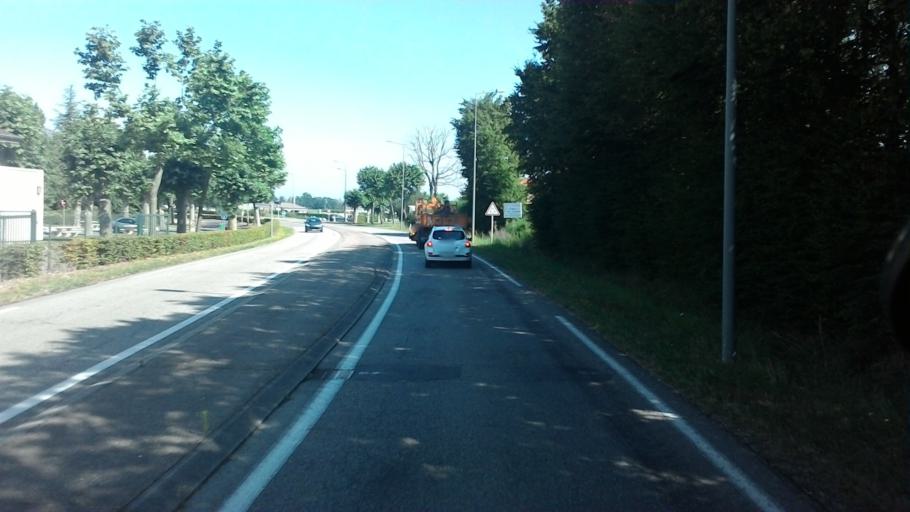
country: FR
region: Rhone-Alpes
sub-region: Departement de l'Ain
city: Saint-Trivier-de-Courtes
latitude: 46.4590
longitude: 5.0843
